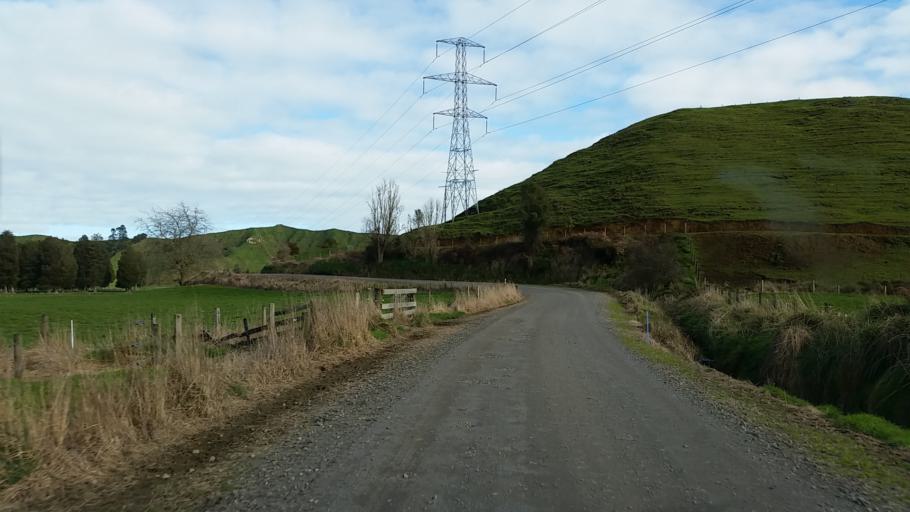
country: NZ
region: Taranaki
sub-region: South Taranaki District
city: Eltham
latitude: -39.2568
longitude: 174.5174
